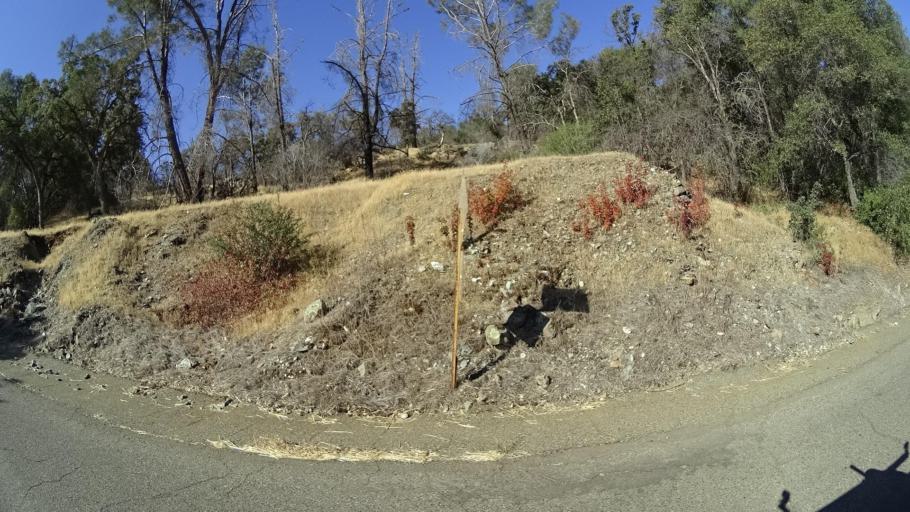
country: US
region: California
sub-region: Mariposa County
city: Mariposa
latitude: 37.5734
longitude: -120.1709
